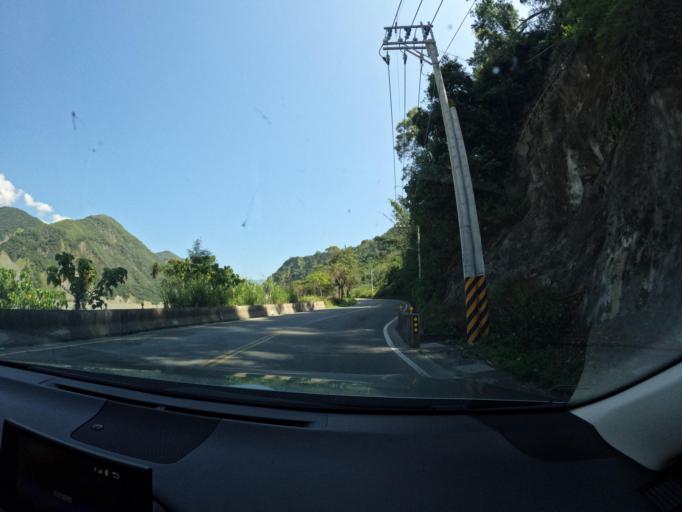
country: TW
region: Taiwan
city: Yujing
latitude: 23.1761
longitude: 120.7788
